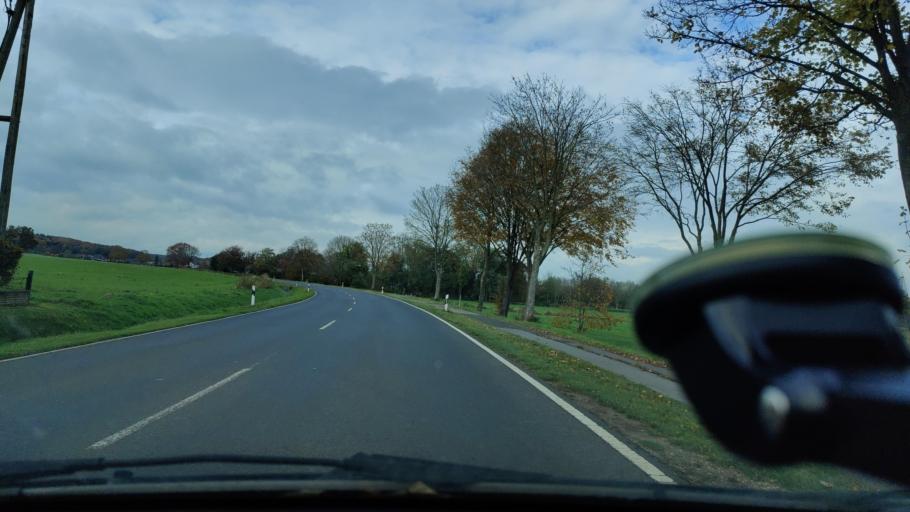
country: DE
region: North Rhine-Westphalia
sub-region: Regierungsbezirk Dusseldorf
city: Sonsbeck
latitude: 51.6398
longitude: 6.3916
